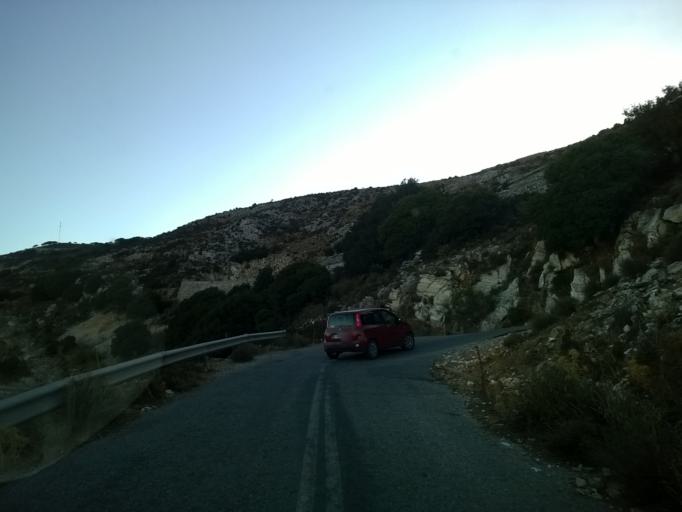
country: GR
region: South Aegean
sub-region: Nomos Kykladon
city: Filotion
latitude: 37.0463
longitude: 25.5044
